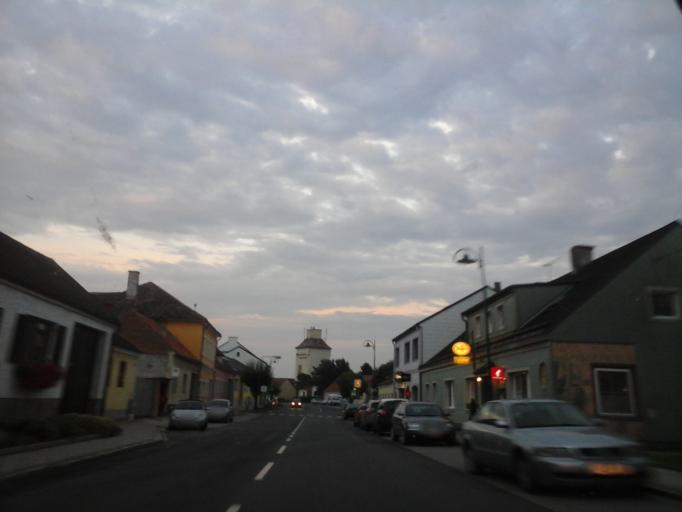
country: AT
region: Lower Austria
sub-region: Politischer Bezirk Bruck an der Leitha
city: Prellenkirchen
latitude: 48.0749
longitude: 16.9505
